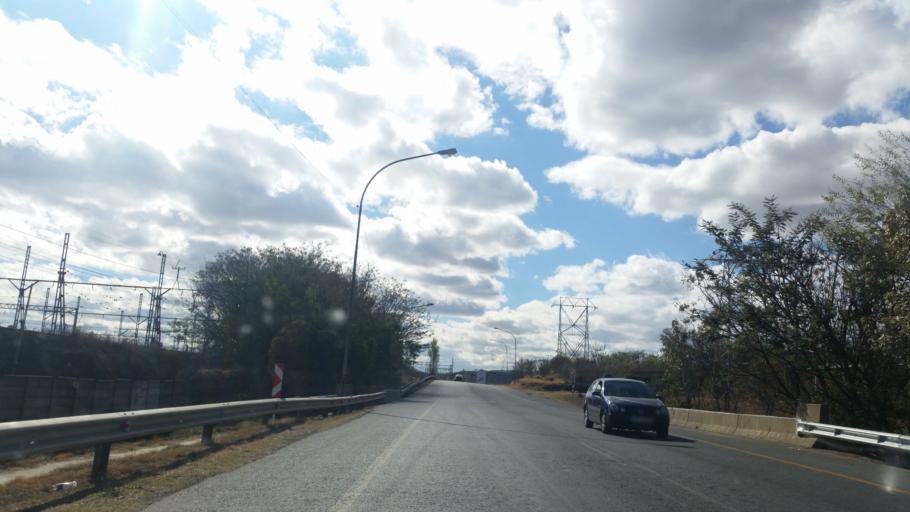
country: ZA
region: KwaZulu-Natal
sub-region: uThukela District Municipality
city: Ladysmith
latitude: -28.5433
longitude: 29.7945
